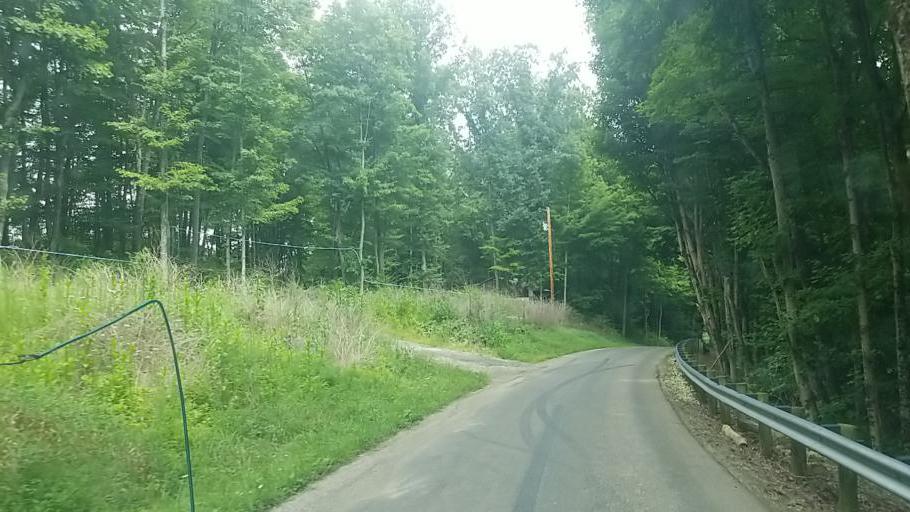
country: US
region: Ohio
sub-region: Licking County
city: Utica
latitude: 40.2467
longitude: -82.2971
